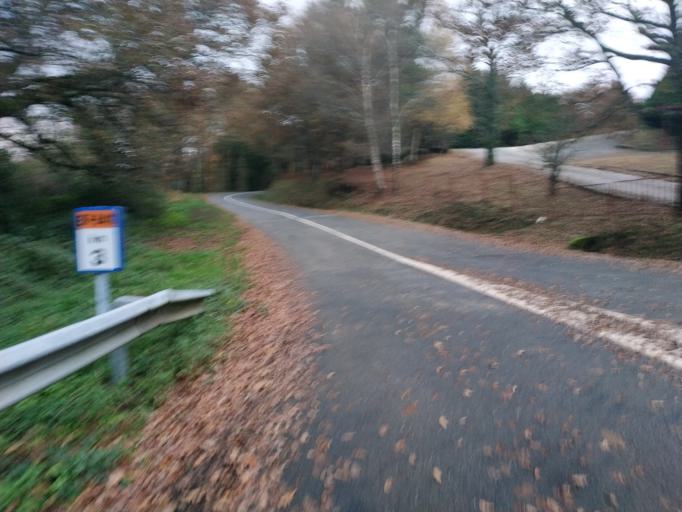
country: ES
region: Galicia
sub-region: Provincia de Pontevedra
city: Silleda
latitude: 42.7788
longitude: -8.1769
